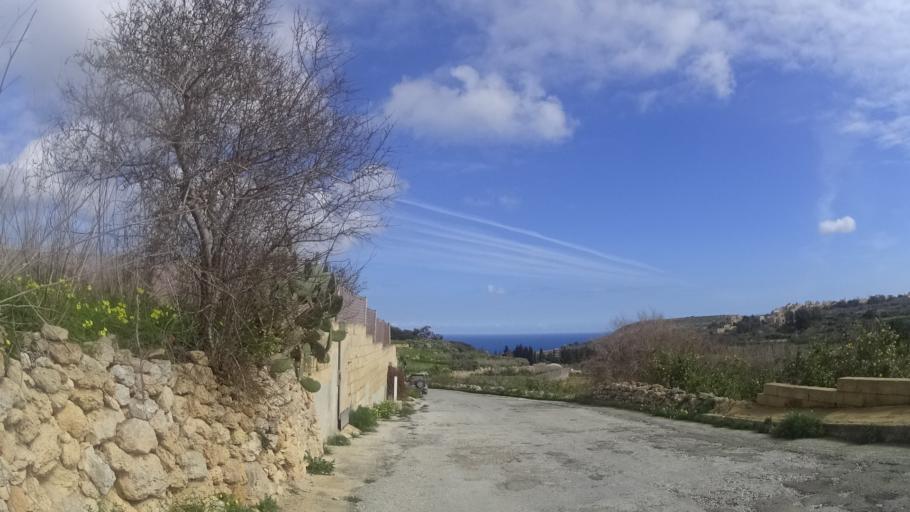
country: MT
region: In-Nadur
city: Nadur
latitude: 36.0437
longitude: 14.3010
